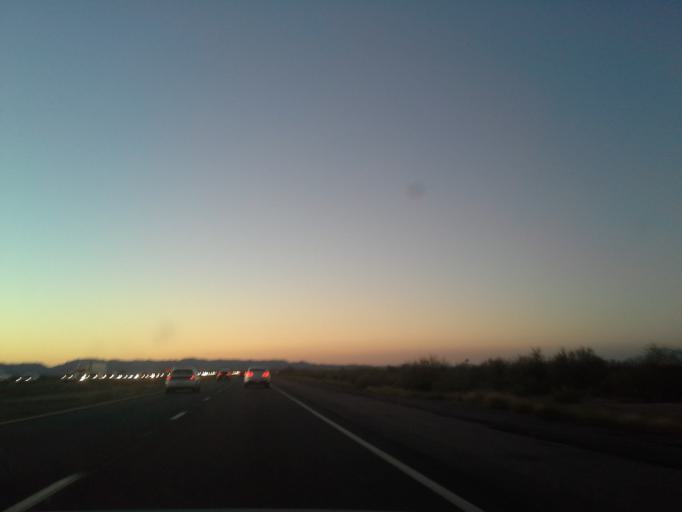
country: US
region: Arizona
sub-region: Maricopa County
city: Sun Lakes
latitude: 33.2093
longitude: -111.9122
